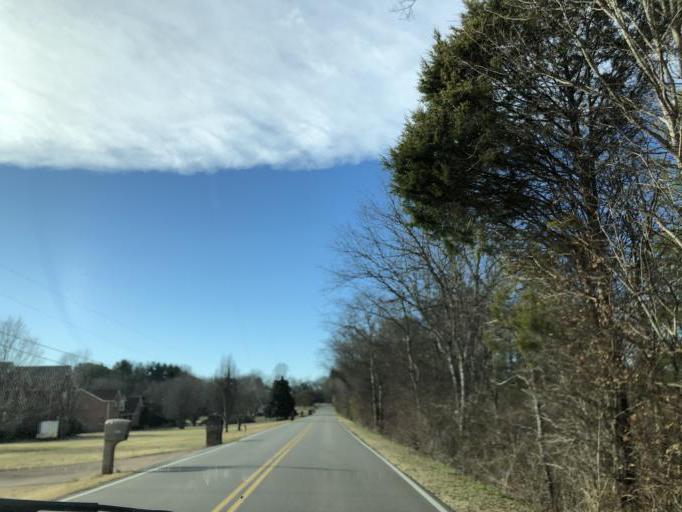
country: US
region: Tennessee
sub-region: Wilson County
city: Mount Juliet
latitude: 36.1672
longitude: -86.5463
